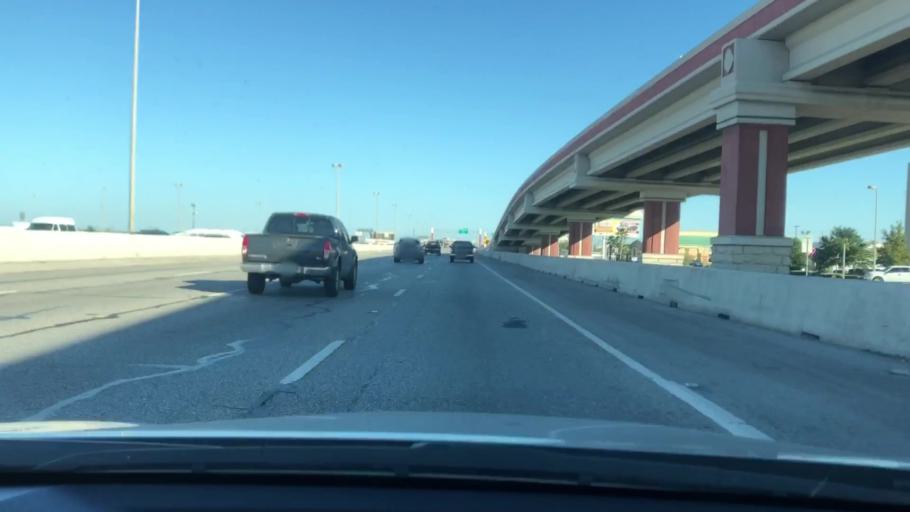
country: US
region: Texas
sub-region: Bexar County
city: Alamo Heights
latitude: 29.5194
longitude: -98.4749
